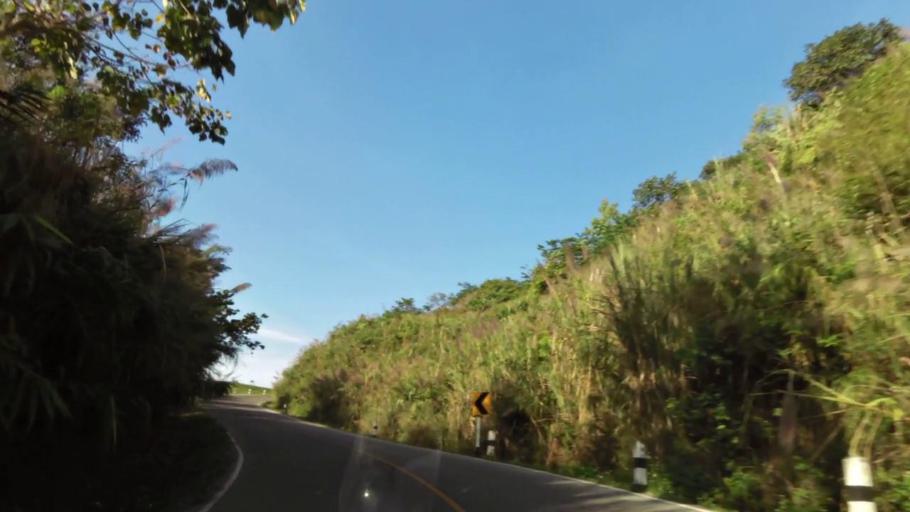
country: TH
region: Chiang Rai
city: Khun Tan
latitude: 19.8480
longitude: 100.4423
